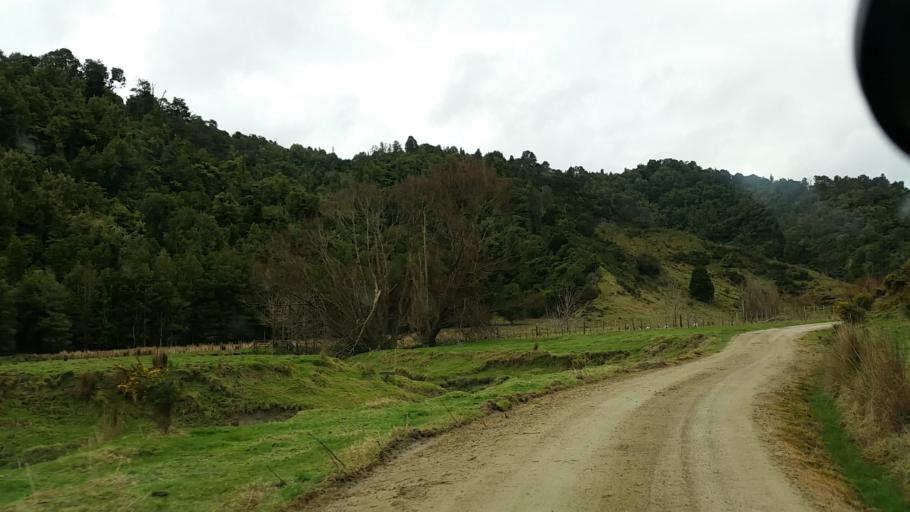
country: NZ
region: Taranaki
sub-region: South Taranaki District
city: Patea
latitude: -39.6575
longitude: 174.7520
